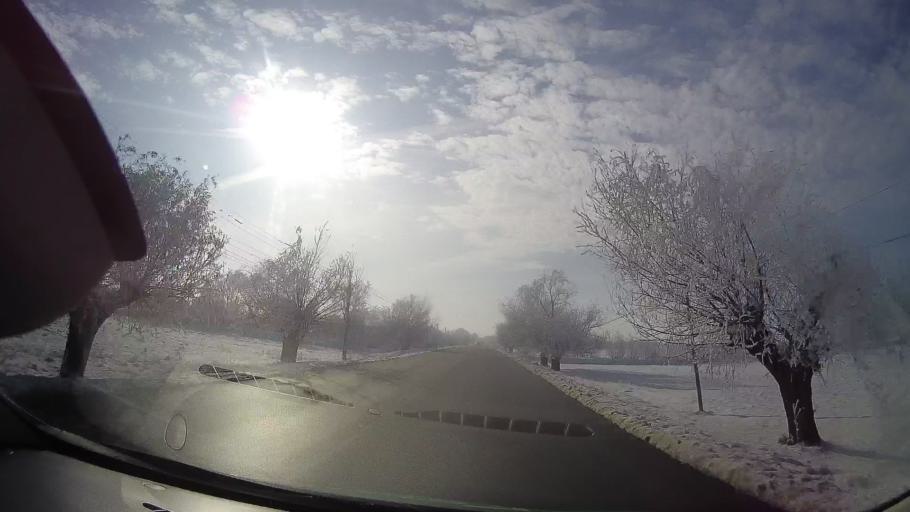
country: RO
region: Neamt
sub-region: Comuna Timisesti
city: Timisesti
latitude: 47.2402
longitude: 26.5389
